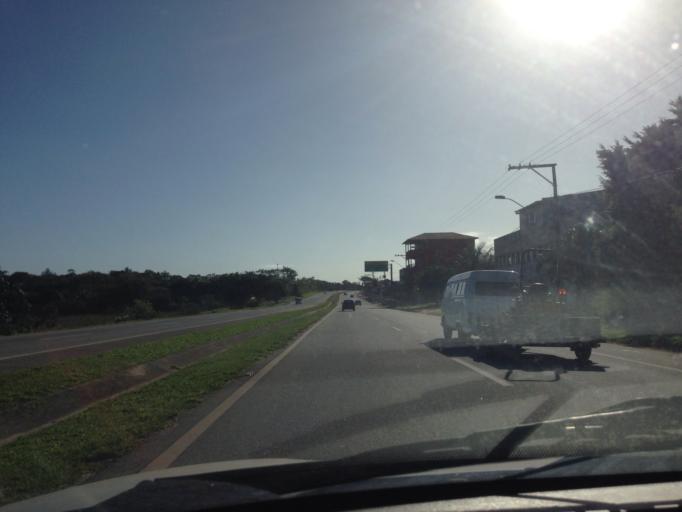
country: BR
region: Espirito Santo
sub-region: Guarapari
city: Guarapari
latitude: -20.5343
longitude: -40.3865
